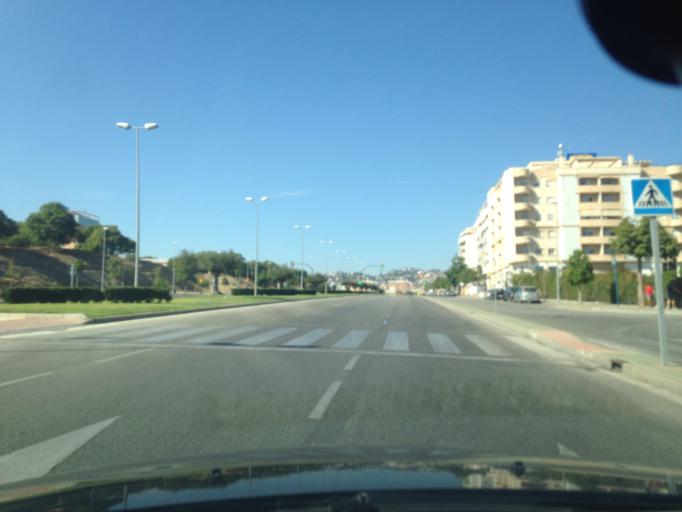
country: ES
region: Andalusia
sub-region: Provincia de Malaga
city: Malaga
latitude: 36.7135
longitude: -4.4665
